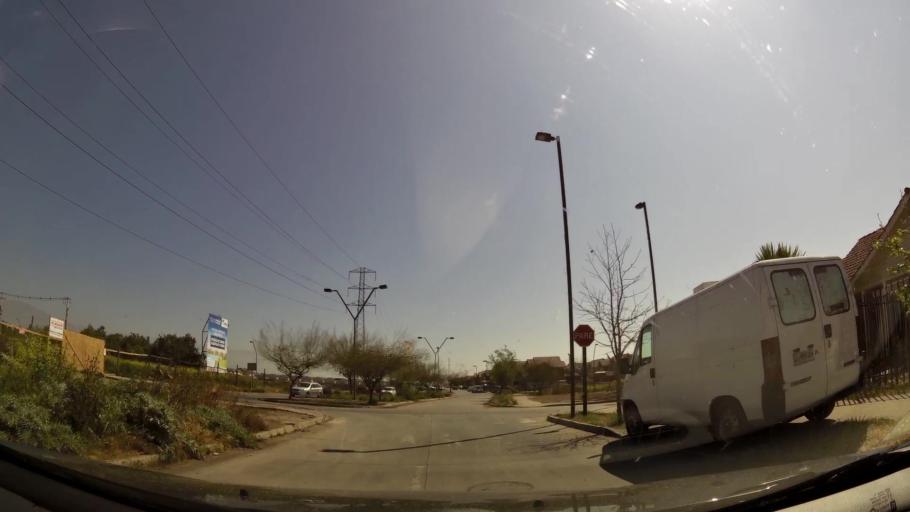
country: CL
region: Santiago Metropolitan
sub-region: Provincia de Chacabuco
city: Chicureo Abajo
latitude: -33.3276
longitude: -70.7539
